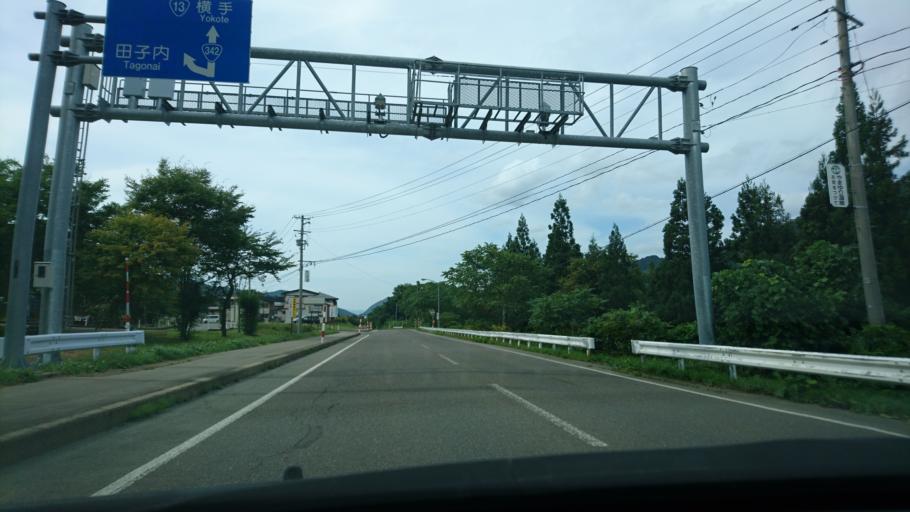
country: JP
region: Akita
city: Yuzawa
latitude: 39.1794
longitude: 140.6556
